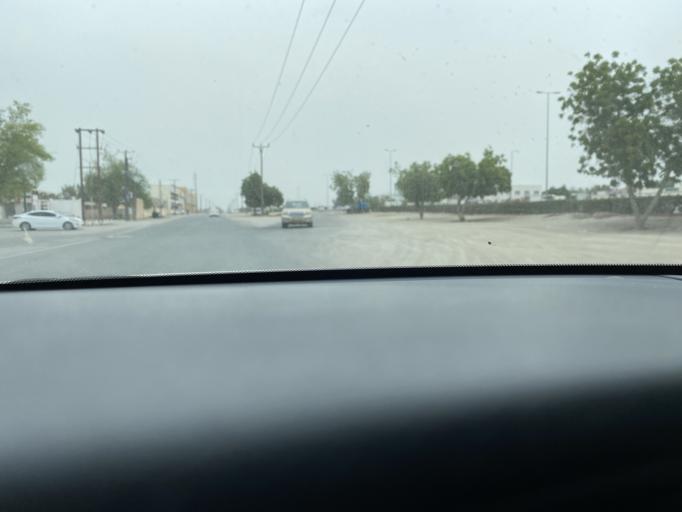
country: OM
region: Al Batinah
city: Barka'
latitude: 23.6971
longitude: 57.7820
